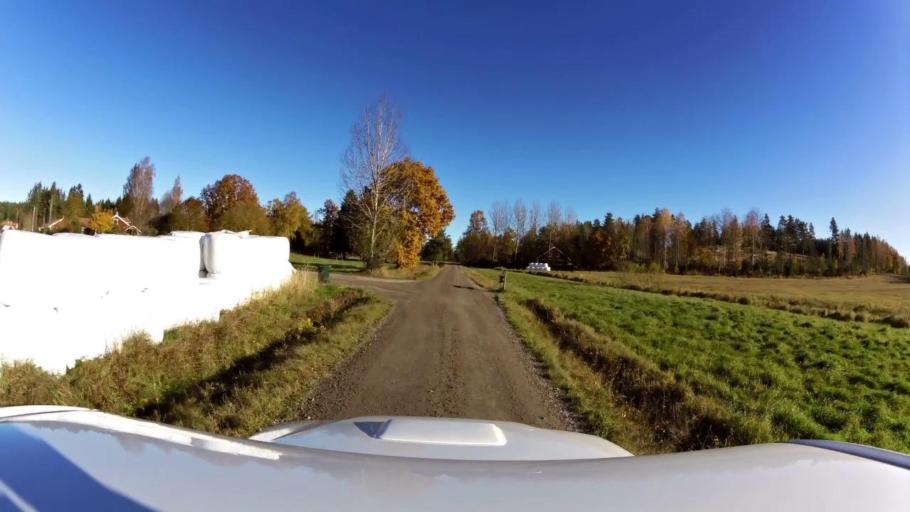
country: SE
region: OEstergoetland
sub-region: Linkopings Kommun
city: Ljungsbro
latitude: 58.5281
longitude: 15.4942
